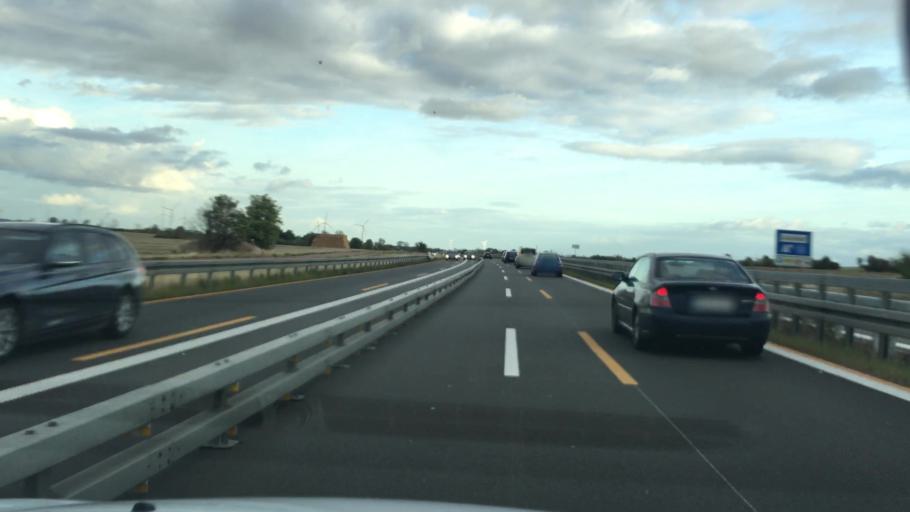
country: DE
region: Saxony-Anhalt
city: Konnern
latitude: 51.6906
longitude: 11.7429
